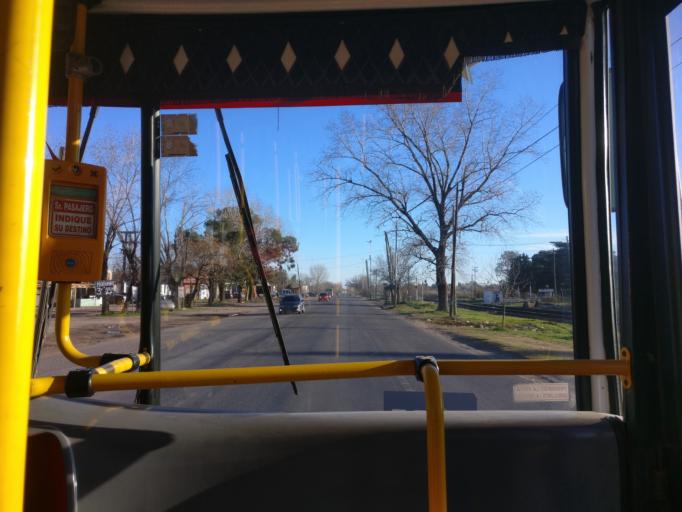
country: AR
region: Buenos Aires
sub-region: Partido de Ezeiza
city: Ezeiza
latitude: -34.9023
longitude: -58.5841
